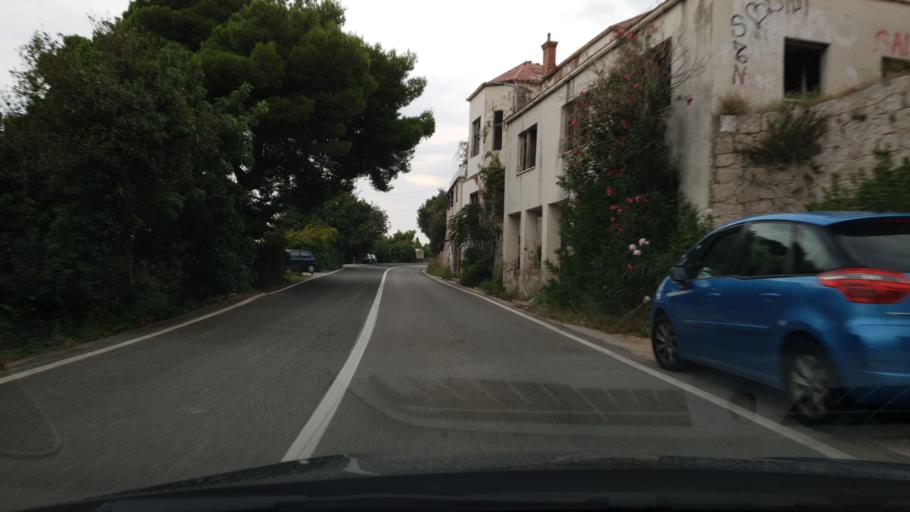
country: HR
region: Dubrovacko-Neretvanska
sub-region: Grad Dubrovnik
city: Mokosica
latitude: 42.6730
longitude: 18.0681
